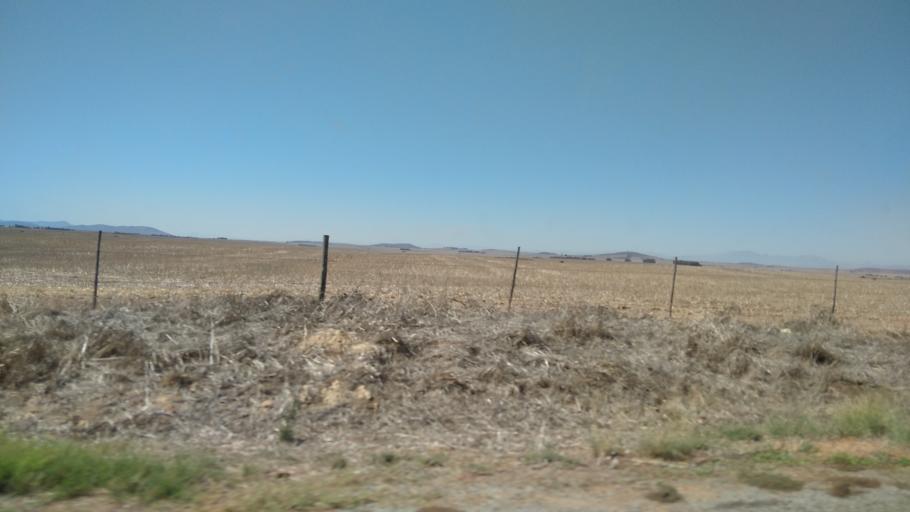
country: ZA
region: Western Cape
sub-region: West Coast District Municipality
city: Moorreesburg
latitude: -33.2262
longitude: 18.5517
